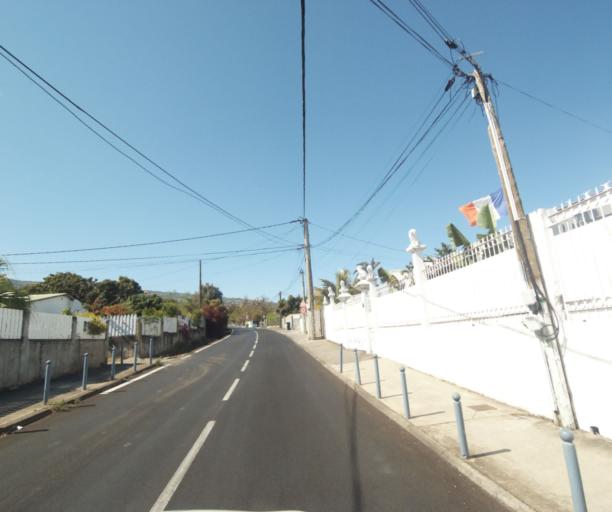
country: RE
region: Reunion
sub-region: Reunion
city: La Possession
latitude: -20.9782
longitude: 55.3240
